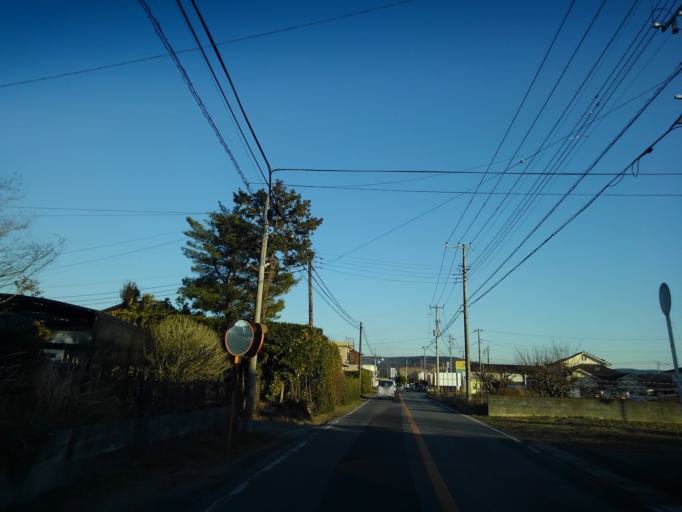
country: JP
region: Chiba
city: Kimitsu
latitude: 35.3045
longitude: 139.9673
